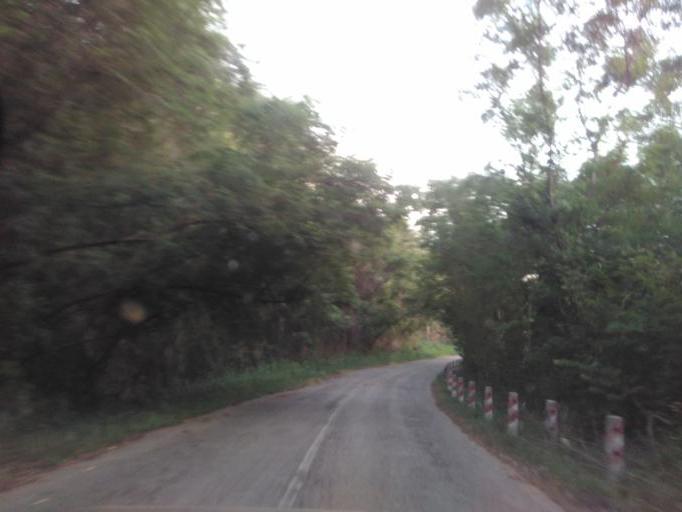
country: GH
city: Bekwai
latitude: 6.5461
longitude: -1.4277
